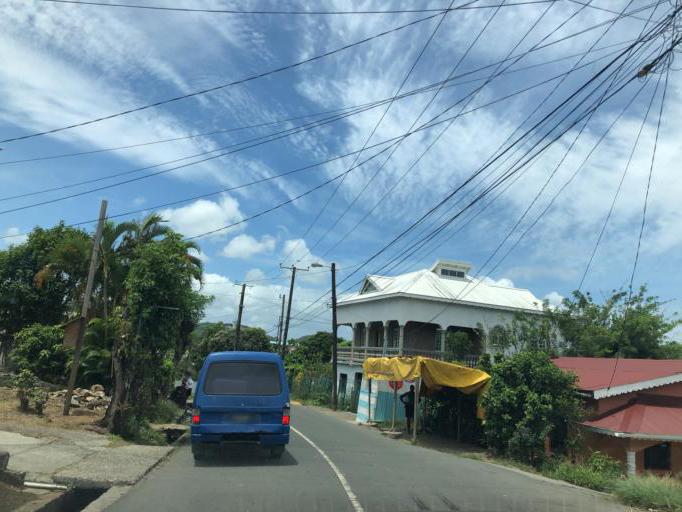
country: LC
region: Castries Quarter
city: Castries
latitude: 13.9933
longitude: -61.0073
